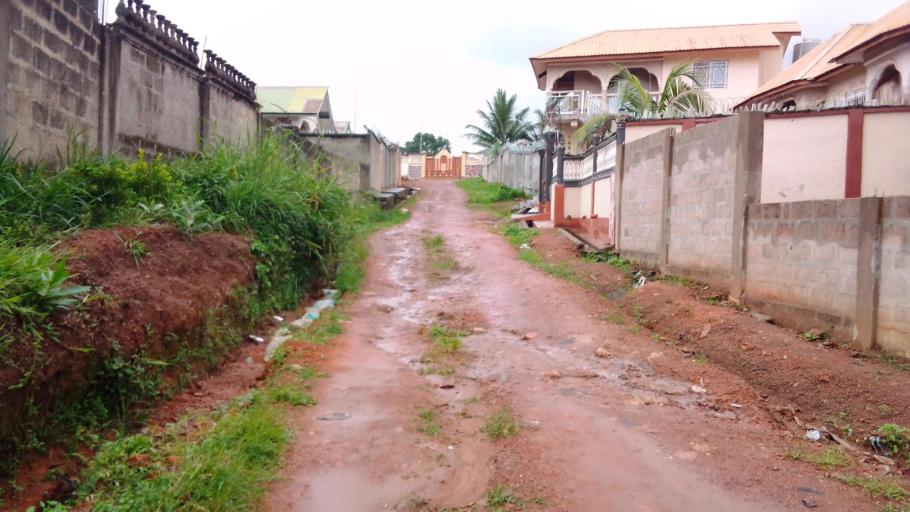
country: SL
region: Eastern Province
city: Kenema
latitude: 7.8755
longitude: -11.1778
